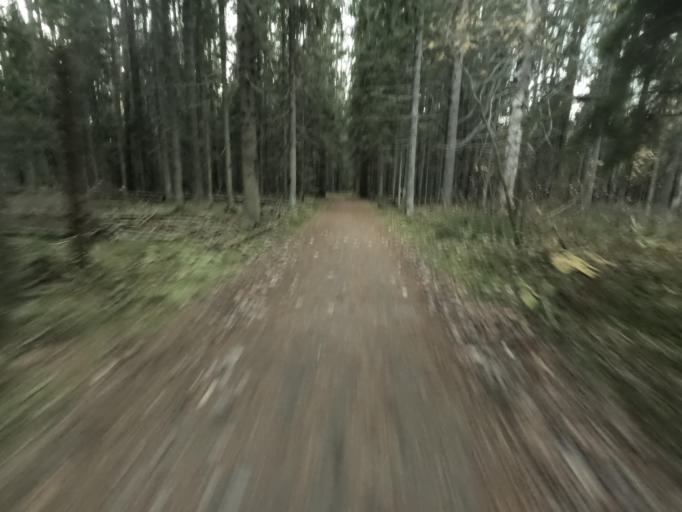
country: RU
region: Leningrad
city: Leninskoye
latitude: 60.1989
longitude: 29.8437
